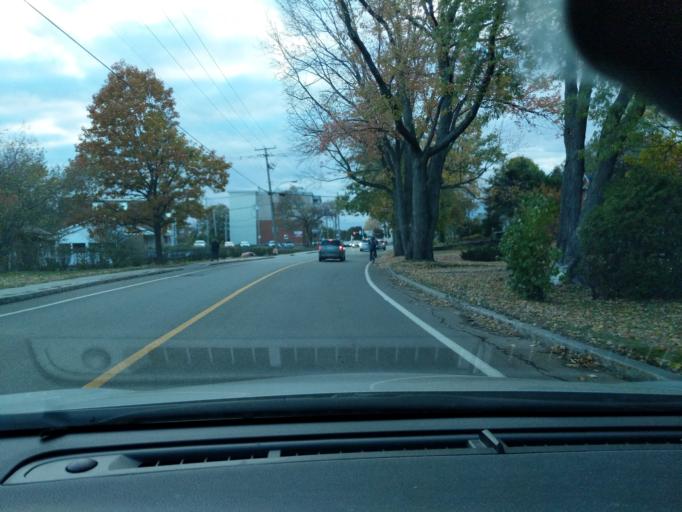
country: CA
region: Quebec
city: L'Ancienne-Lorette
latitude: 46.7635
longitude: -71.2801
